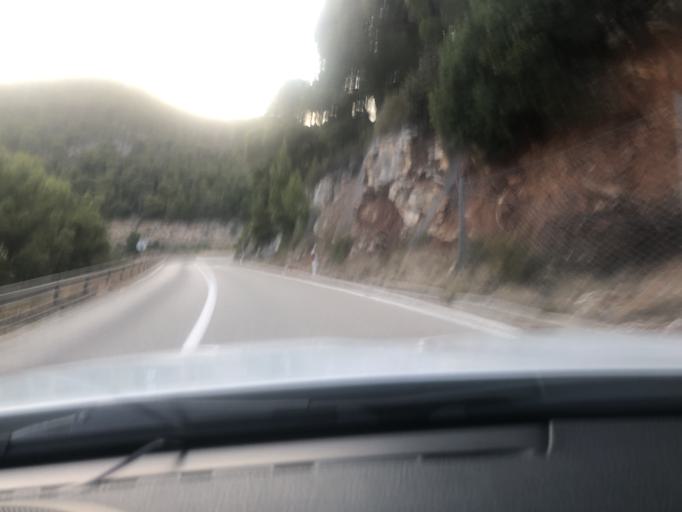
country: HR
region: Splitsko-Dalmatinska
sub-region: Grad Hvar
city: Hvar
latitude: 43.1652
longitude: 16.4842
